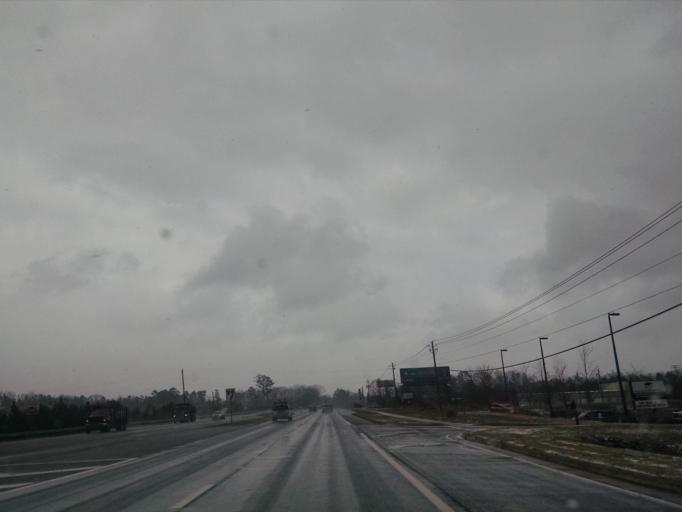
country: US
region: Georgia
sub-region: Gwinnett County
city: Suwanee
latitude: 34.0756
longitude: -84.0618
